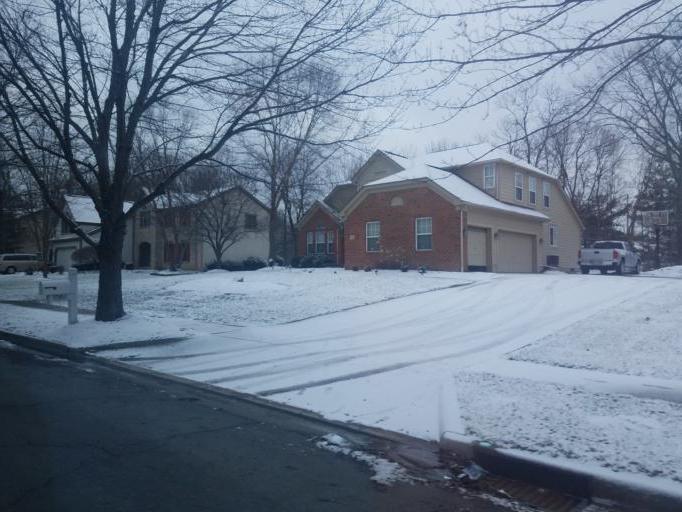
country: US
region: Ohio
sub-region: Franklin County
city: New Albany
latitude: 40.0460
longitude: -82.8315
